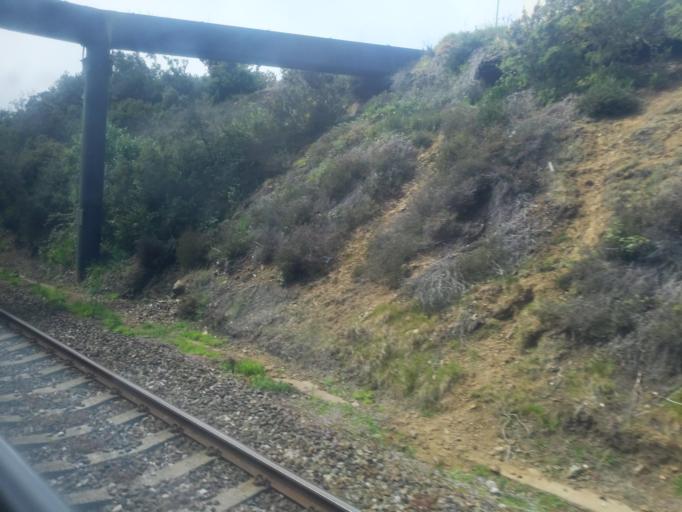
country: GB
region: England
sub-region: Cornwall
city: Camborne
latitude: 50.2134
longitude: -5.2871
